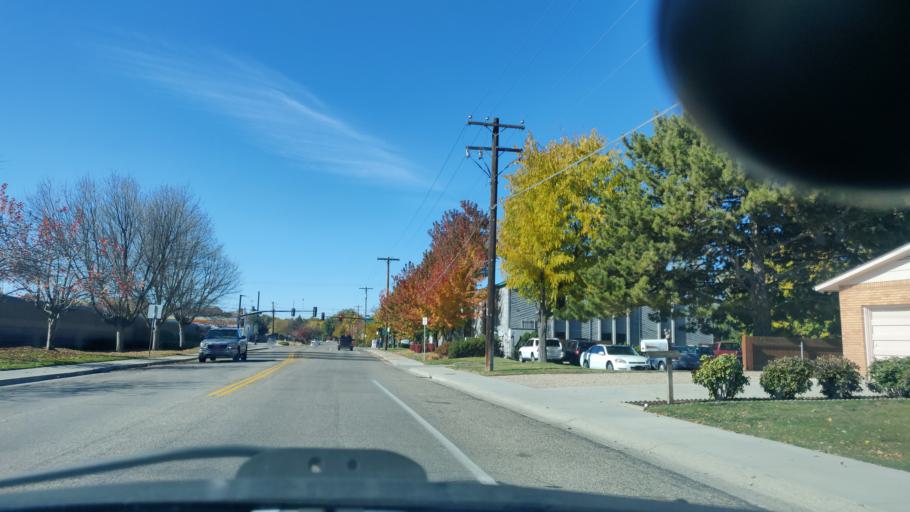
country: US
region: Idaho
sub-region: Ada County
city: Garden City
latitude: 43.5935
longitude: -116.2422
